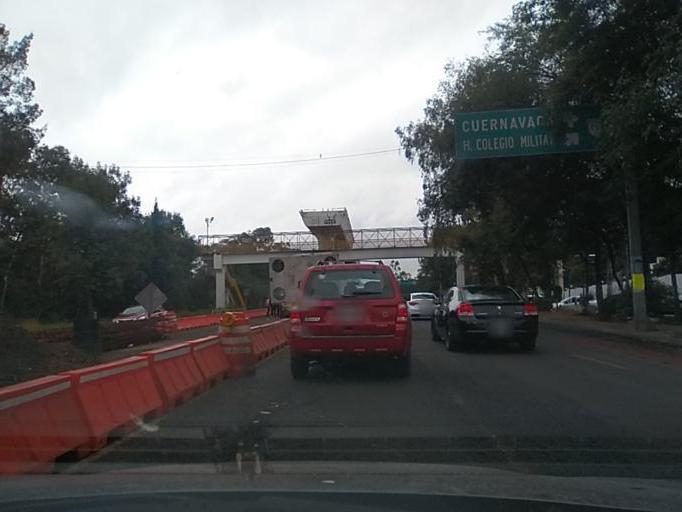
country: MX
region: Mexico City
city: Tlalpan
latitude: 19.2575
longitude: -99.1612
